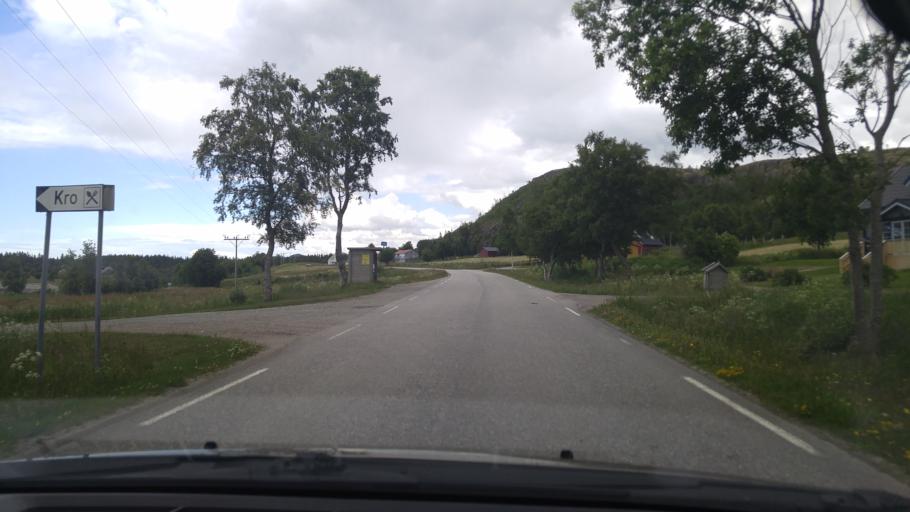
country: NO
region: Nord-Trondelag
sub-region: Fosnes
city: Joa
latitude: 64.6877
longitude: 11.4343
